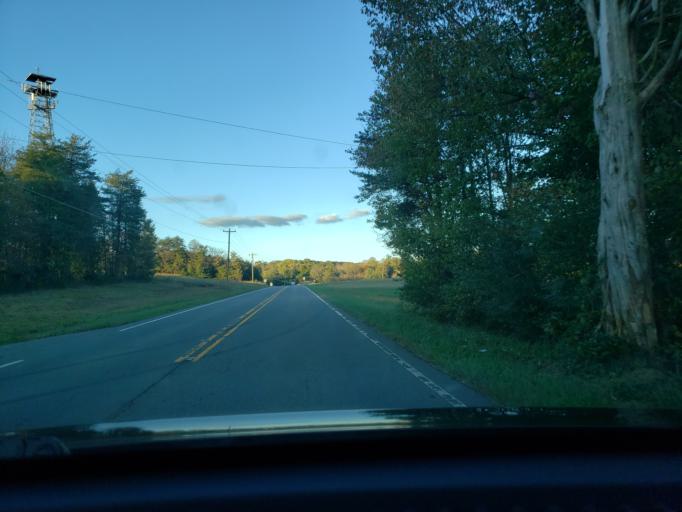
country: US
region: North Carolina
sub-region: Stokes County
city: Danbury
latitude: 36.3374
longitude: -80.2215
